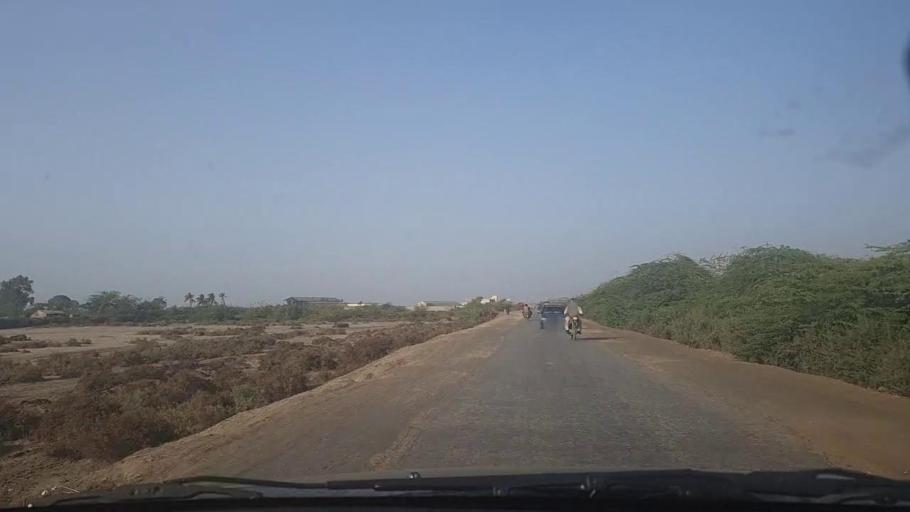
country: PK
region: Sindh
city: Keti Bandar
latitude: 24.3107
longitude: 67.6097
